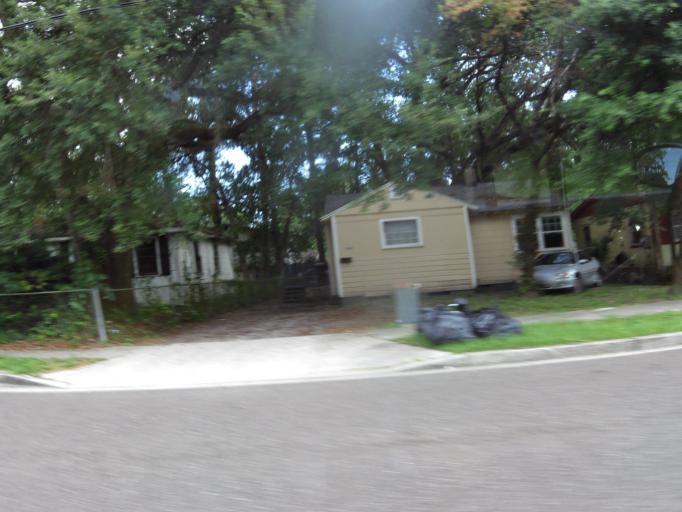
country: US
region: Florida
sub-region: Duval County
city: Jacksonville
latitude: 30.3649
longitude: -81.6826
